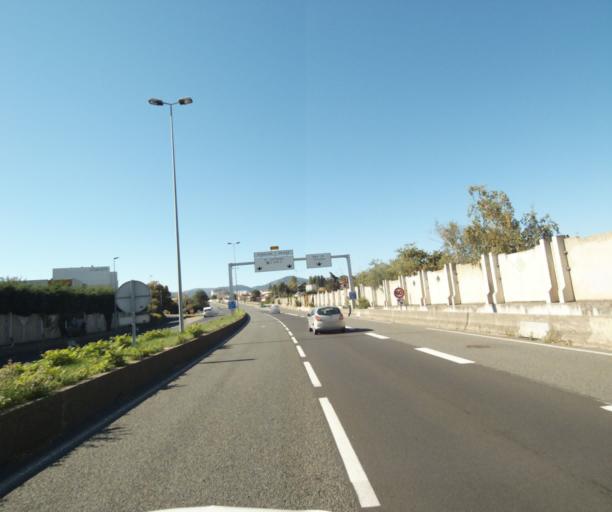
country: FR
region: Auvergne
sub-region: Departement du Puy-de-Dome
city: Aubiere
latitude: 45.7716
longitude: 3.1175
